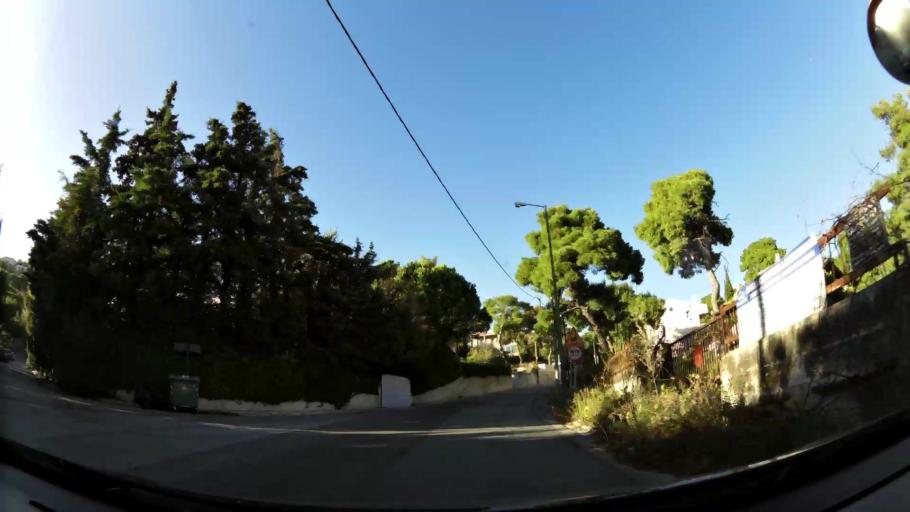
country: GR
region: Attica
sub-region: Nomarchia Athinas
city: Penteli
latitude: 38.0459
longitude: 23.8698
